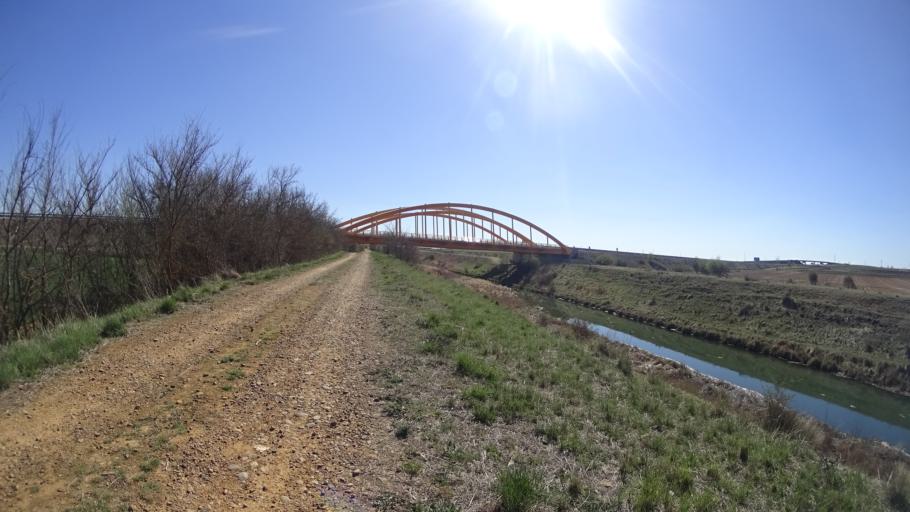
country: ES
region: Castille and Leon
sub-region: Provincia de Palencia
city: Osornillo
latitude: 42.4022
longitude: -4.3438
